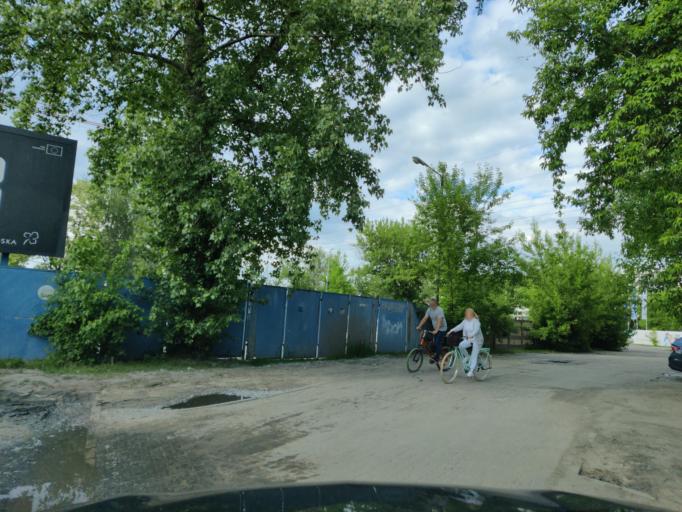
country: PL
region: Masovian Voivodeship
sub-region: Warszawa
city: Praga Poludnie
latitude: 52.2541
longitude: 21.0773
